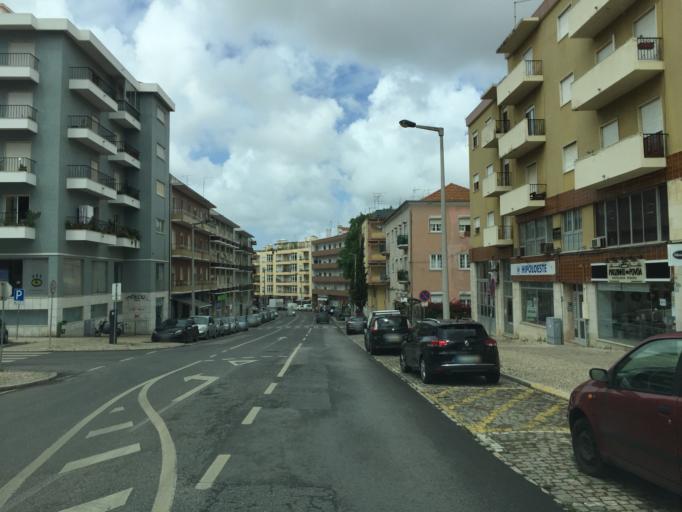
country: PT
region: Lisbon
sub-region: Torres Vedras
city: Torres Vedras
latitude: 39.0874
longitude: -9.2588
